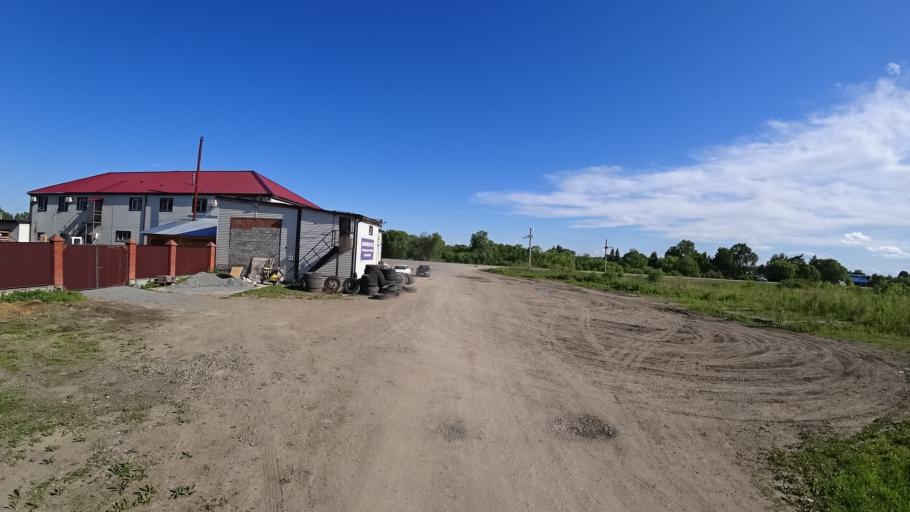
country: RU
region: Khabarovsk Krai
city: Khor
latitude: 47.8922
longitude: 134.9954
